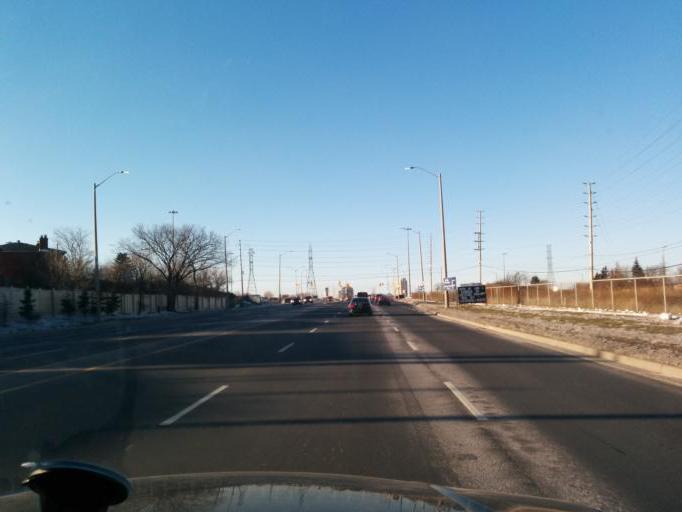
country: CA
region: Ontario
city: Mississauga
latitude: 43.5837
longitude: -79.6572
